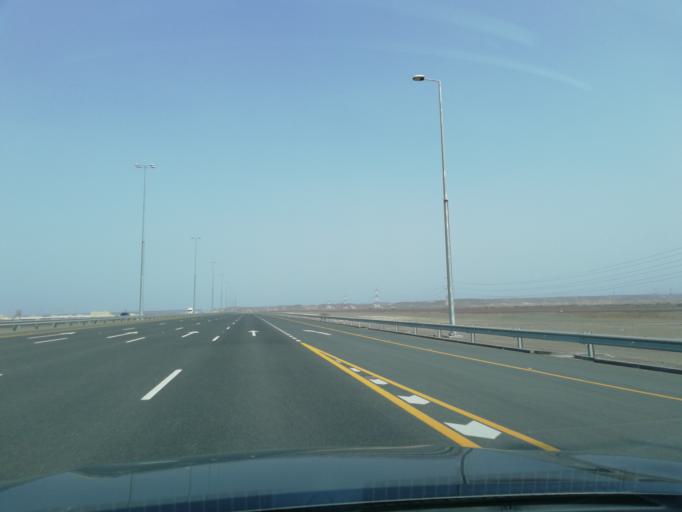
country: OM
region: Al Batinah
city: Al Sohar
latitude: 24.3156
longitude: 56.5800
